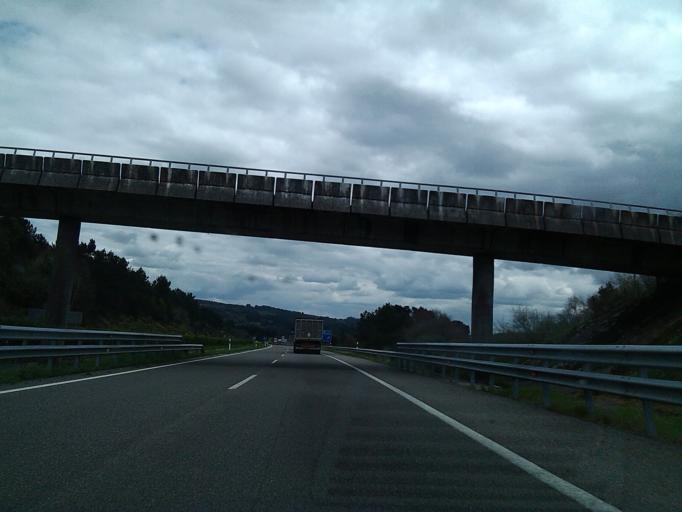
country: ES
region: Galicia
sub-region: Provincia de Lugo
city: Guitiriz
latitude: 43.1861
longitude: -7.8384
